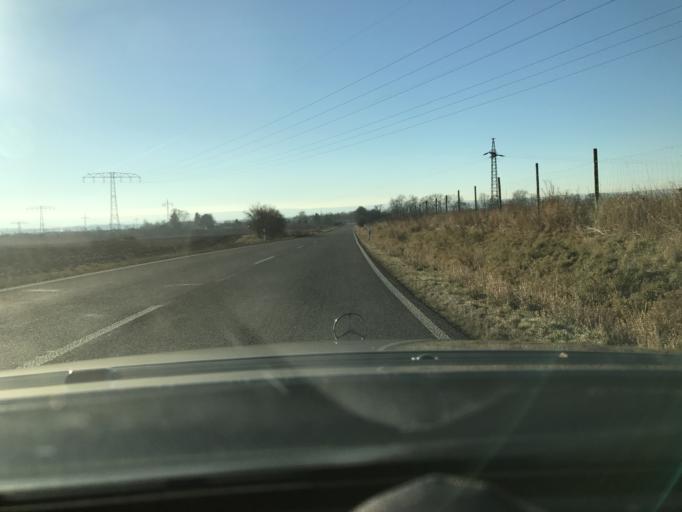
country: DE
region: Thuringia
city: Muehlhausen
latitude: 51.2343
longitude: 10.4832
